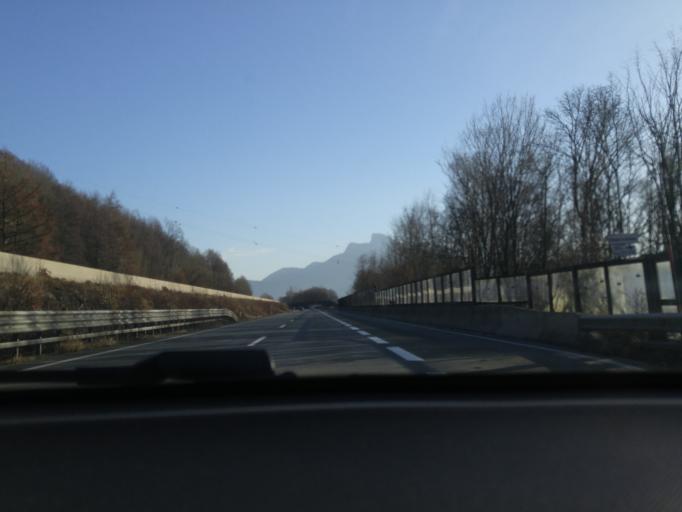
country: AT
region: Upper Austria
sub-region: Politischer Bezirk Vocklabruck
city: Mondsee
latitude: 47.8579
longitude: 13.3542
